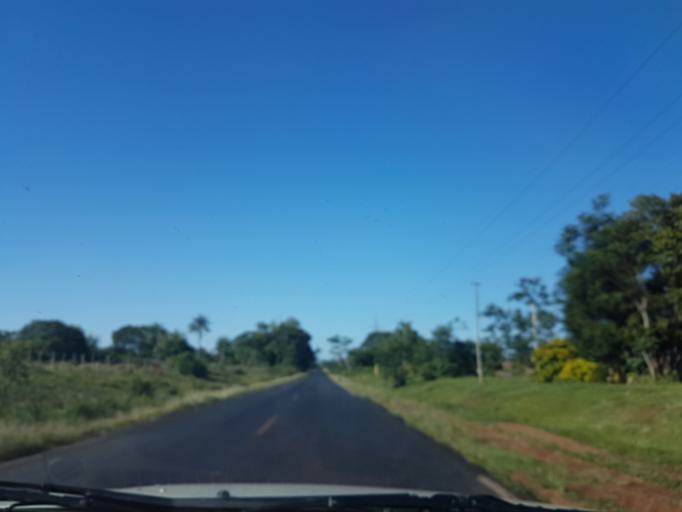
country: PY
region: Cordillera
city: Arroyos y Esteros
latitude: -25.0775
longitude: -57.0941
